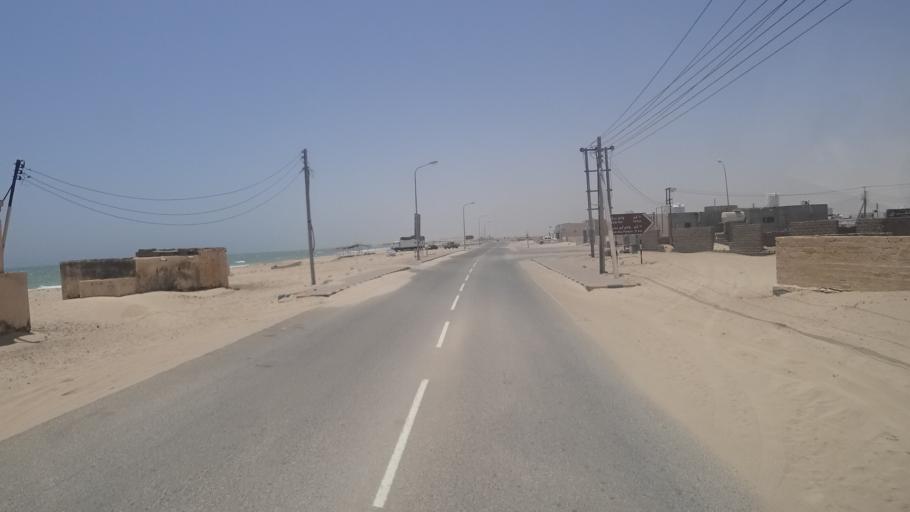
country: OM
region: Ash Sharqiyah
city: Sur
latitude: 22.0802
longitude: 59.6835
